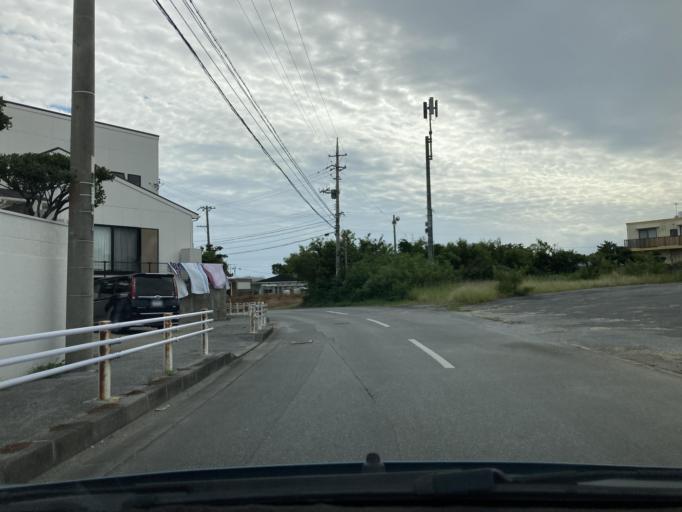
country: JP
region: Okinawa
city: Tomigusuku
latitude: 26.1371
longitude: 127.7906
